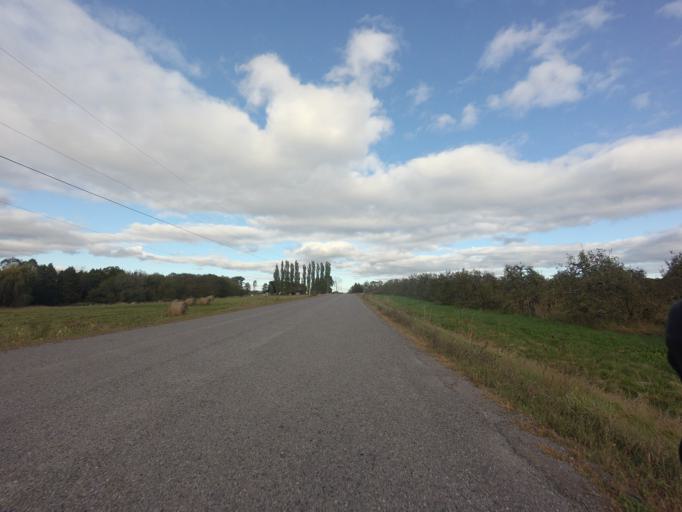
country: CA
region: Ontario
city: Cobourg
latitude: 43.9789
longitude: -77.9948
